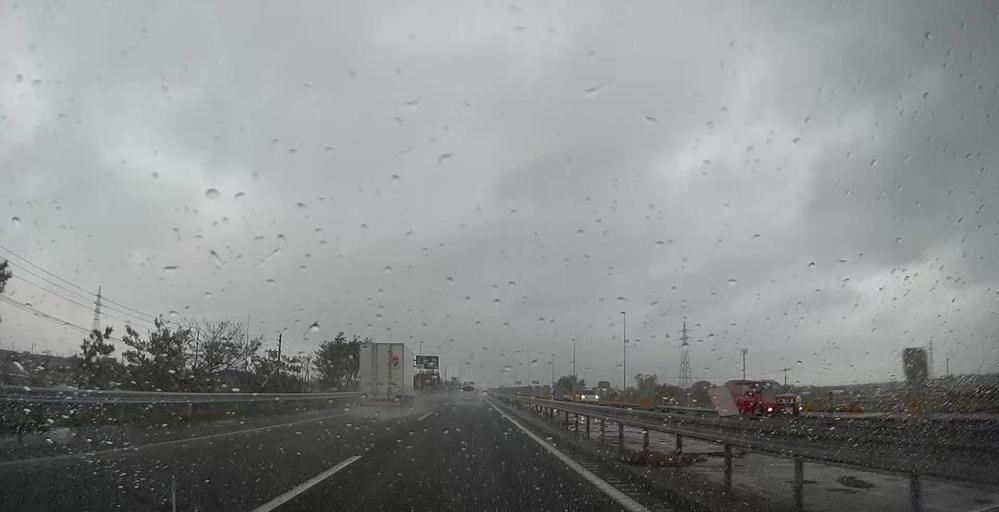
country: JP
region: Niigata
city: Maki
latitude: 37.7413
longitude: 138.9383
